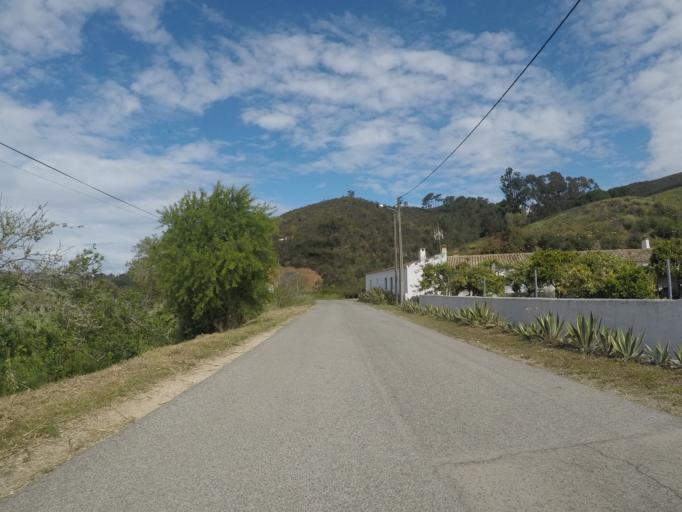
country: PT
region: Beja
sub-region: Odemira
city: Sao Teotonio
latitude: 37.4364
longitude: -8.7675
